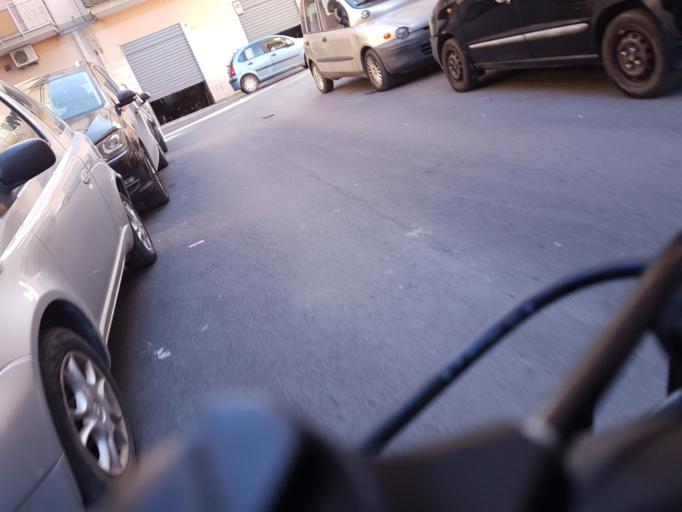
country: IT
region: Apulia
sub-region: Provincia di Bari
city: Corato
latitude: 41.1516
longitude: 16.4185
